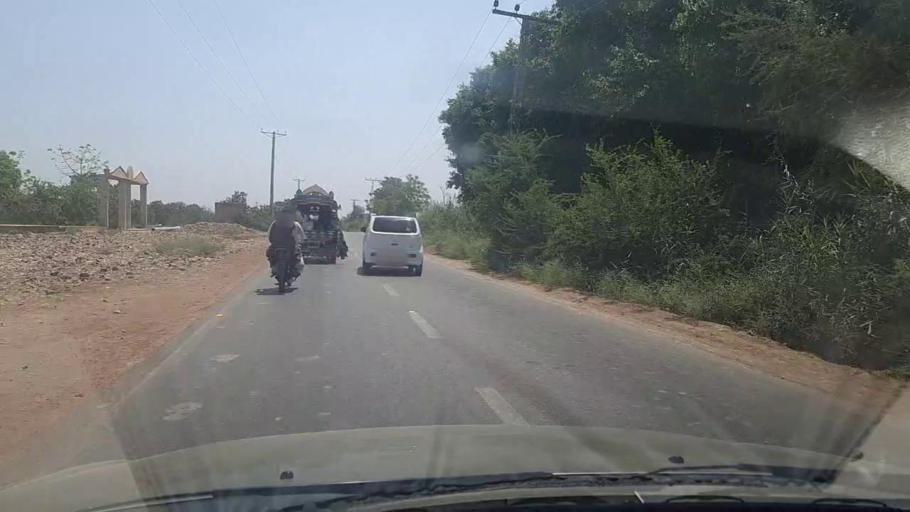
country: PK
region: Sindh
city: Hyderabad
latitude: 25.3908
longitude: 68.4087
